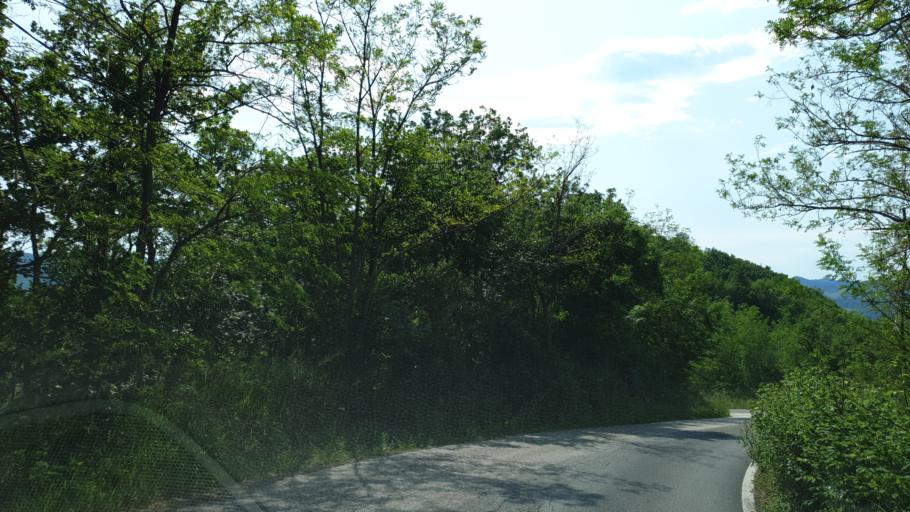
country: IT
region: Emilia-Romagna
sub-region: Provincia di Rimini
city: Sant'Agata Feltria
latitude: 43.9121
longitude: 12.1988
